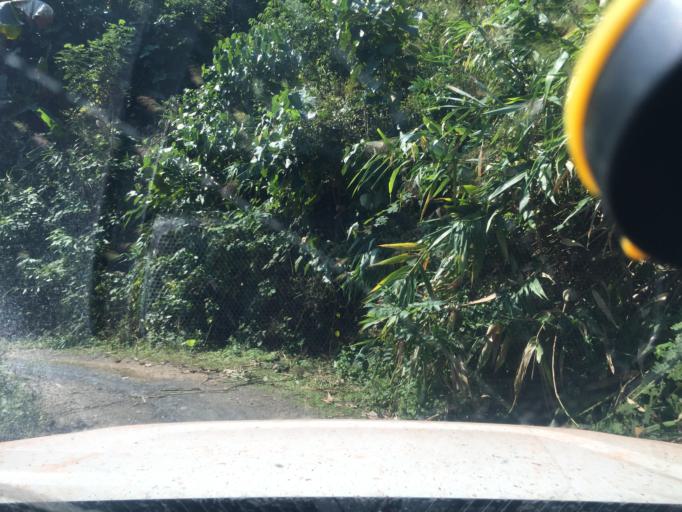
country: LA
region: Phongsali
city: Phongsali
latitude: 21.6872
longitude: 102.4087
